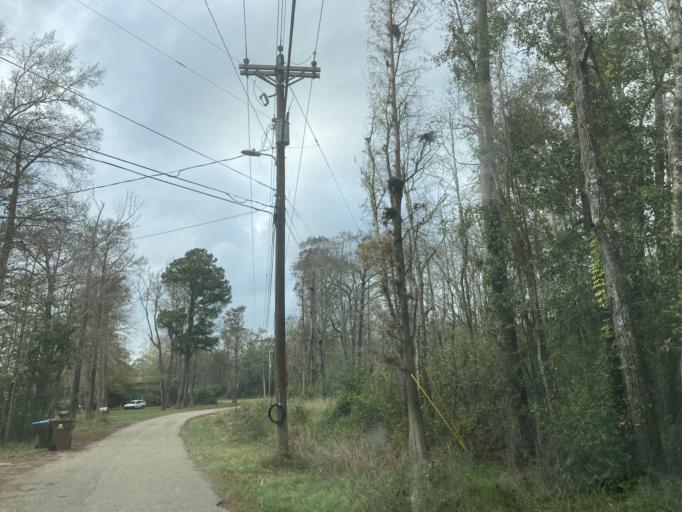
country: US
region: Mississippi
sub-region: Harrison County
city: West Gulfport
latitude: 30.4766
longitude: -89.0169
